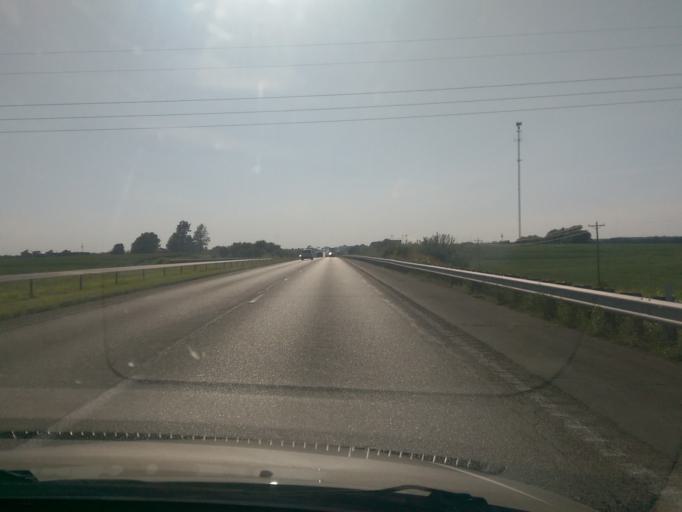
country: US
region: Missouri
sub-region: Lafayette County
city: Odessa
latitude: 39.0061
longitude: -93.8966
